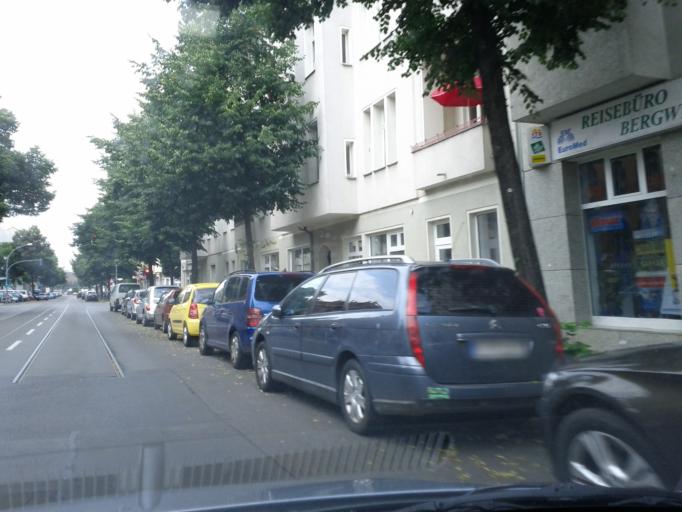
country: DE
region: Berlin
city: Niederschoneweide
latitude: 52.4549
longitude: 13.5152
